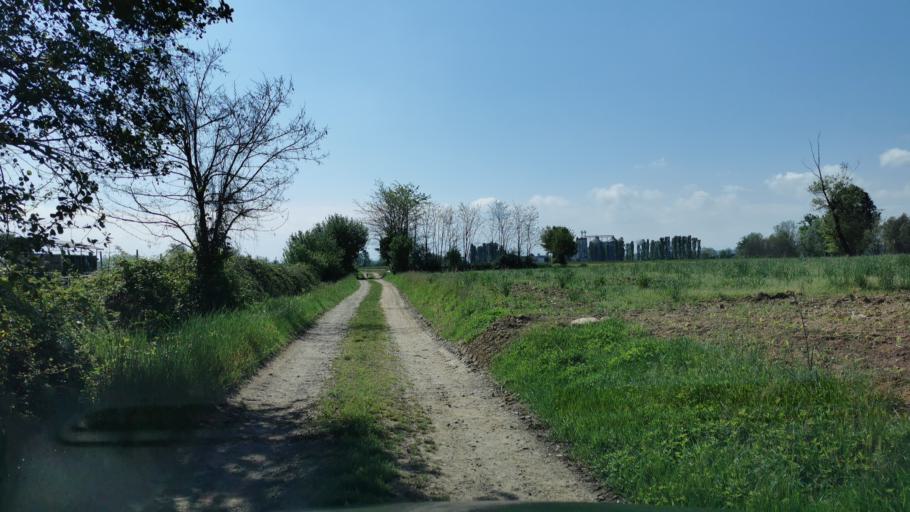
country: IT
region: Piedmont
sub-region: Provincia di Torino
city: Feletto
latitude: 45.2871
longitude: 7.7199
